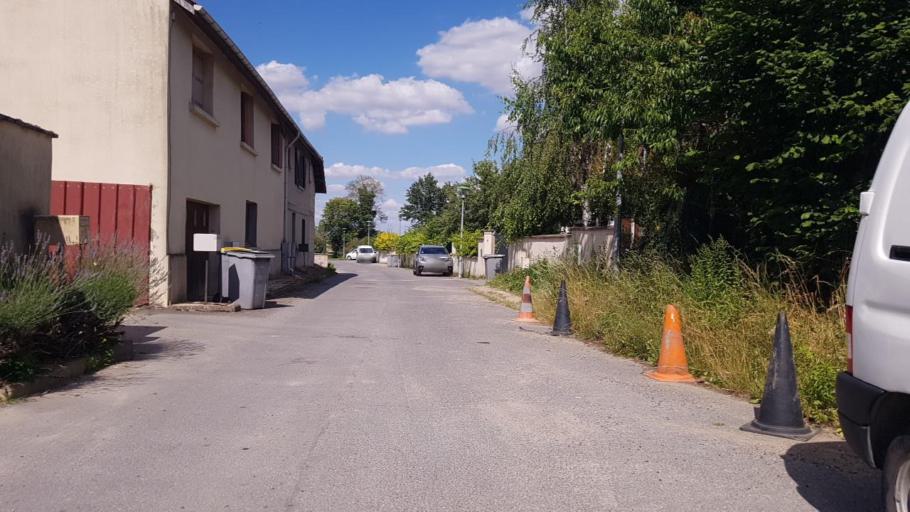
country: FR
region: Ile-de-France
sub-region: Departement de Seine-et-Marne
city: Othis
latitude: 49.0850
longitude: 2.6540
